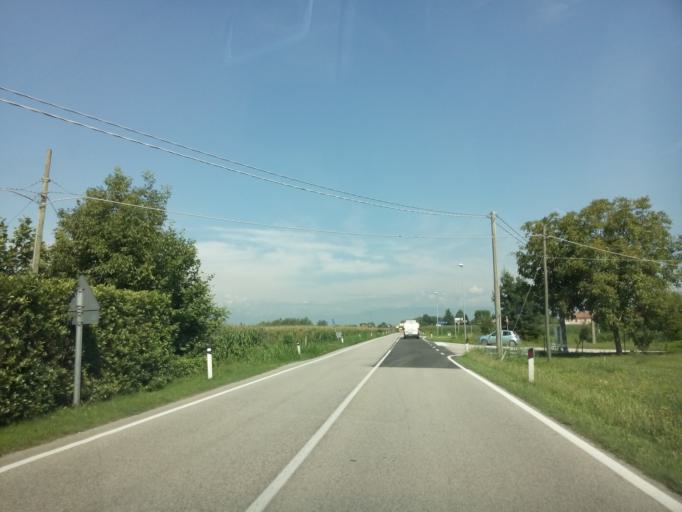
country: IT
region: Veneto
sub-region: Provincia di Padova
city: Piazzola sul Brenta
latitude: 45.5547
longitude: 11.7659
